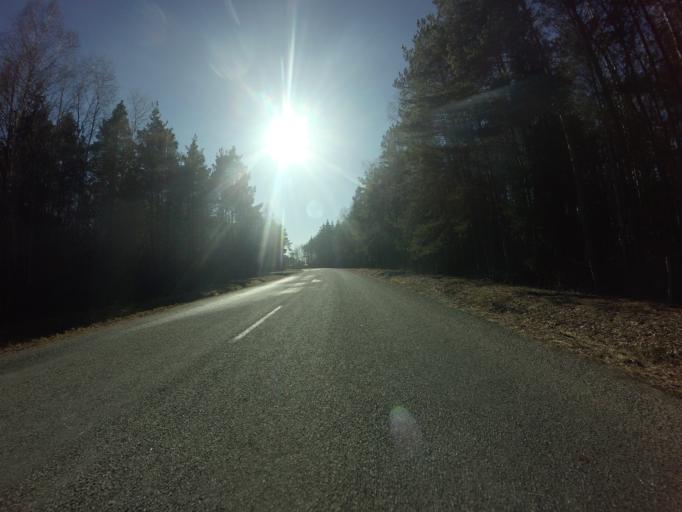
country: EE
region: Saare
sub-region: Kuressaare linn
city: Kuressaare
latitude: 58.5030
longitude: 22.3066
